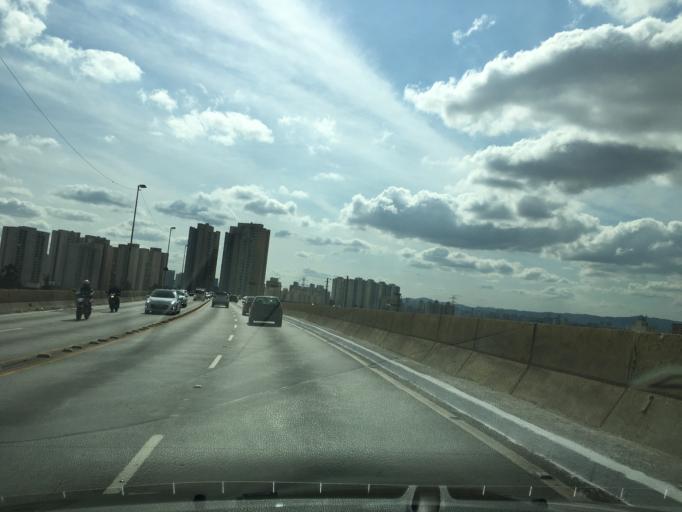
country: BR
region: Sao Paulo
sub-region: Guarulhos
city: Guarulhos
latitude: -23.5330
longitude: -46.5495
